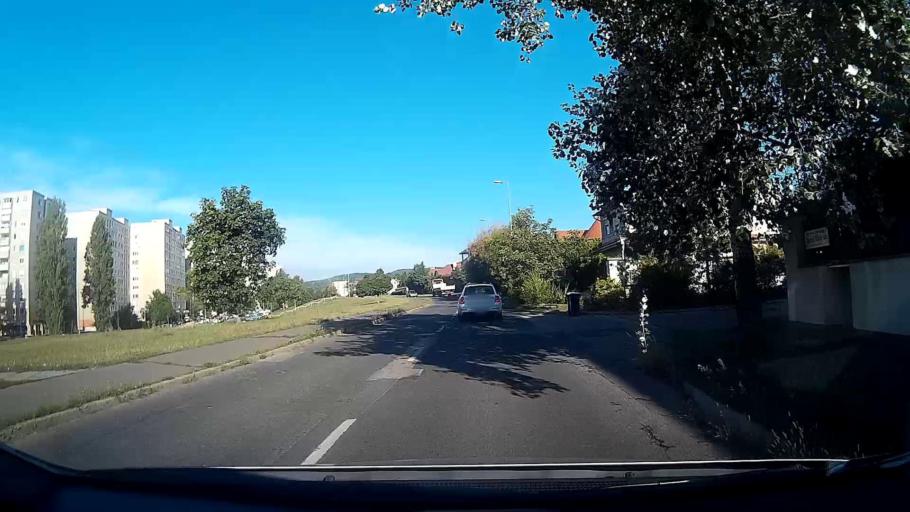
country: HU
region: Pest
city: Budakalasz
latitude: 47.6020
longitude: 19.0545
